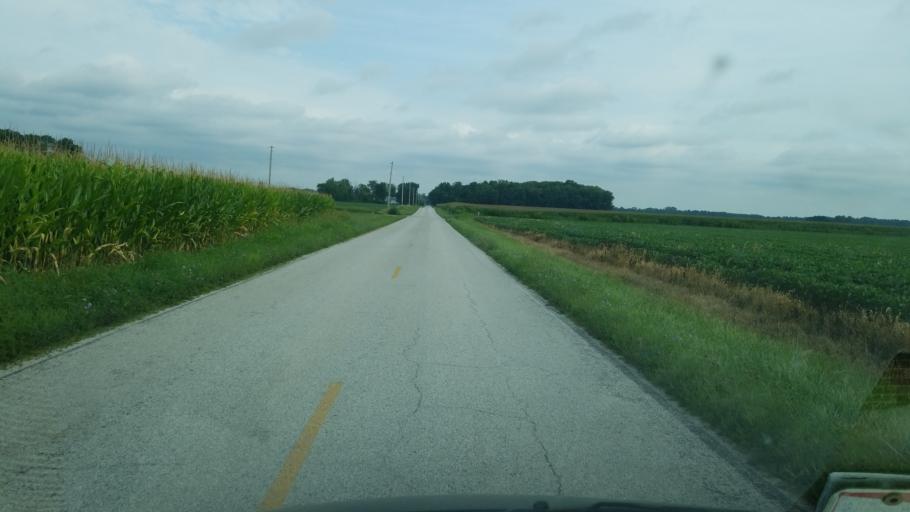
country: US
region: Ohio
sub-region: Seneca County
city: Tiffin
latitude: 41.1709
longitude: -83.1031
